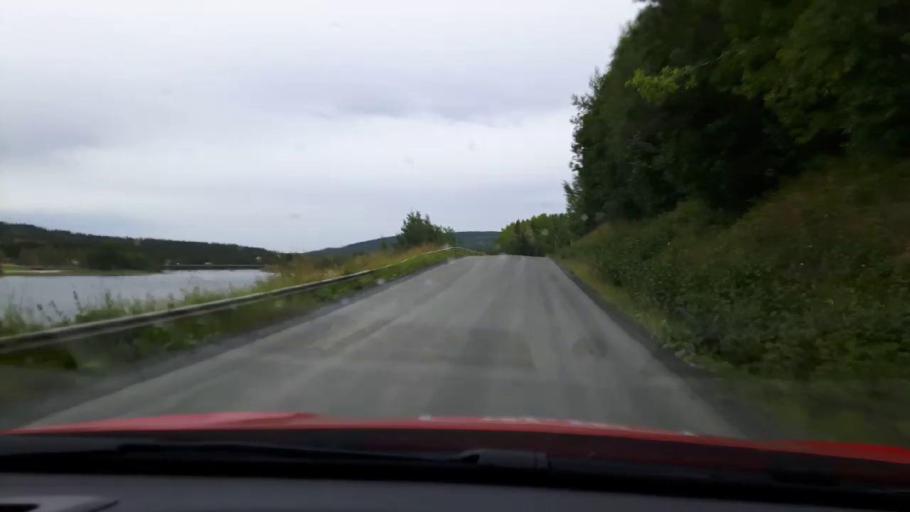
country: SE
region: Jaemtland
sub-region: Are Kommun
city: Jarpen
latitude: 63.4122
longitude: 13.3571
